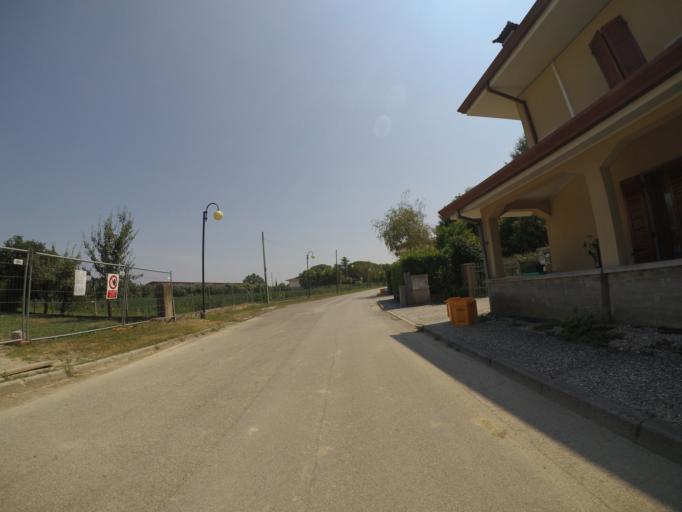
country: IT
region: Friuli Venezia Giulia
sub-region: Provincia di Udine
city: Varmo
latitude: 45.9042
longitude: 12.9989
